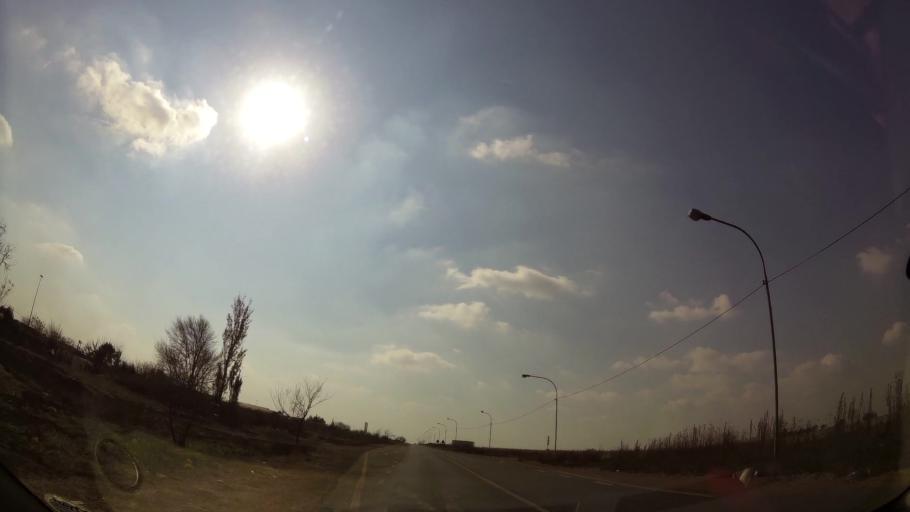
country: ZA
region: Gauteng
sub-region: Ekurhuleni Metropolitan Municipality
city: Springs
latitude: -26.1309
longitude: 28.4844
